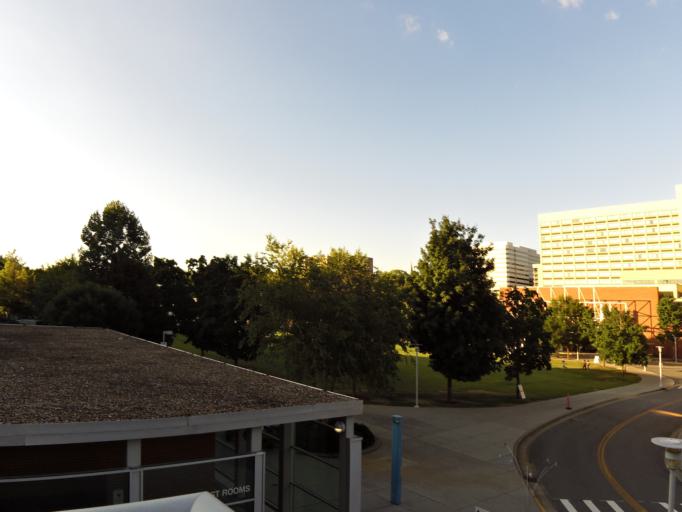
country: US
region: Tennessee
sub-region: Knox County
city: Knoxville
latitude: 35.9618
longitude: -83.9244
